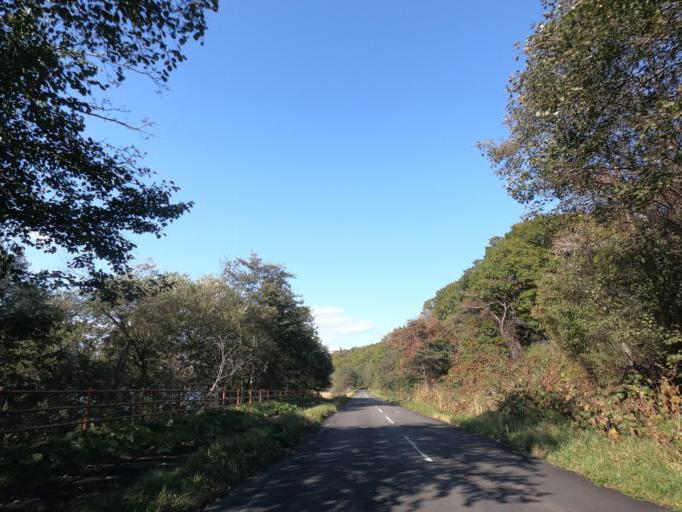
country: JP
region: Hokkaido
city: Obihiro
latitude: 42.6117
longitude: 143.5444
